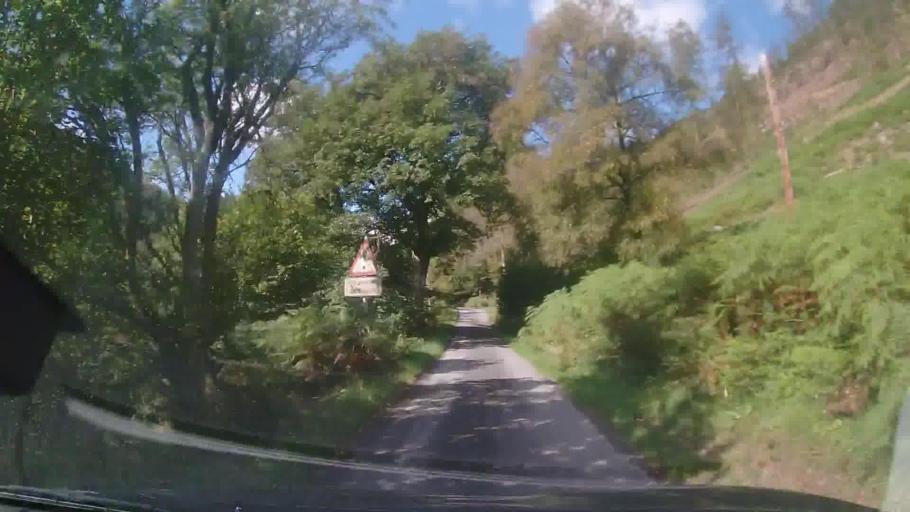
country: GB
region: Wales
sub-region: Gwynedd
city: Bala
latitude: 52.7900
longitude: -3.5406
